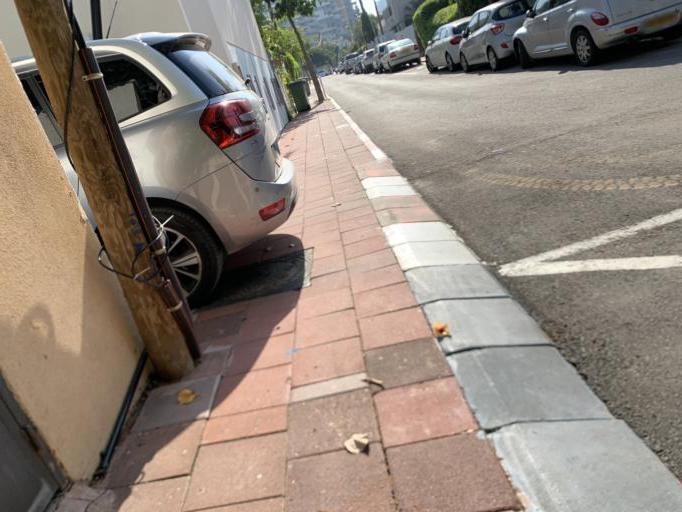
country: IL
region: Tel Aviv
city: Ramat Gan
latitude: 32.0930
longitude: 34.8127
